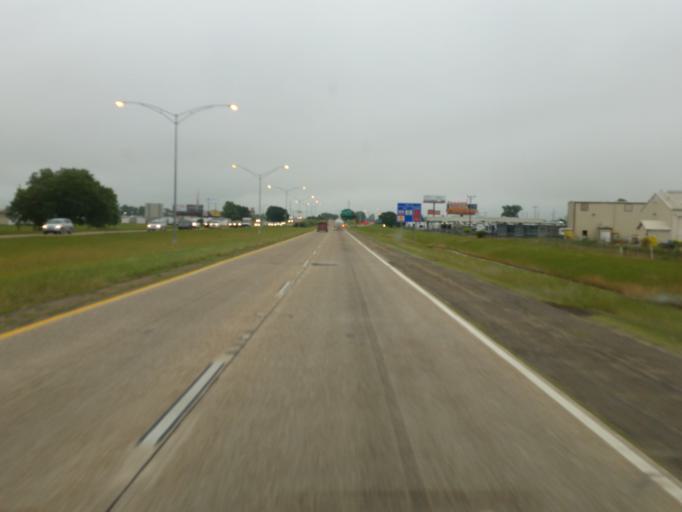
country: US
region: Louisiana
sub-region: Bossier Parish
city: Bossier City
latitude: 32.5269
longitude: -93.6816
